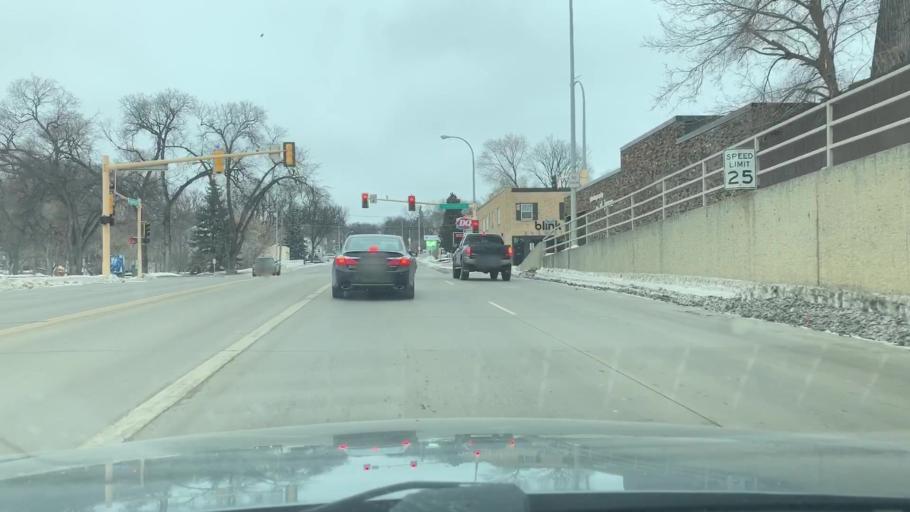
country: US
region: North Dakota
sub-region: Burleigh County
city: Bismarck
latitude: 46.8061
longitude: -100.7944
